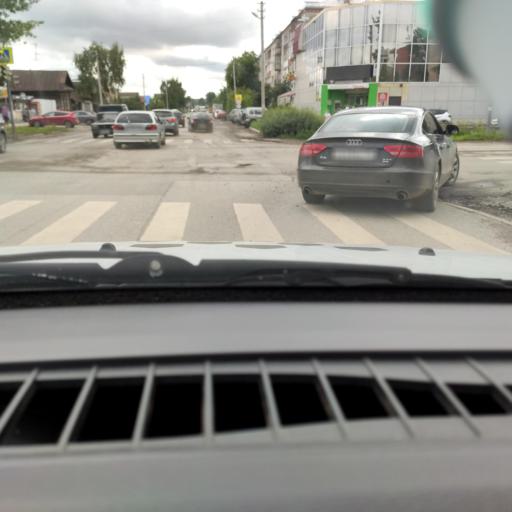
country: RU
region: Sverdlovsk
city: Krasnoufimsk
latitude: 56.6150
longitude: 57.7760
